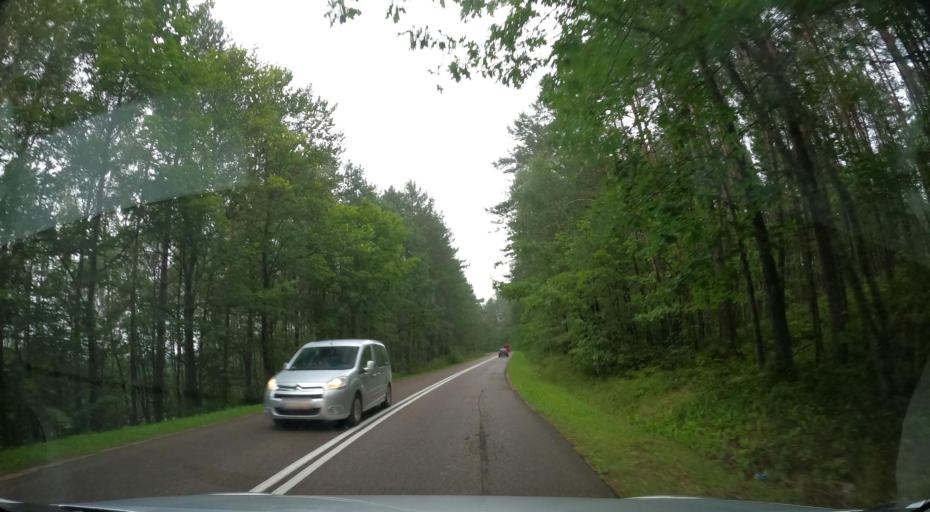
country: PL
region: Pomeranian Voivodeship
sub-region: Powiat wejherowski
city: Luzino
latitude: 54.4786
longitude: 18.0949
